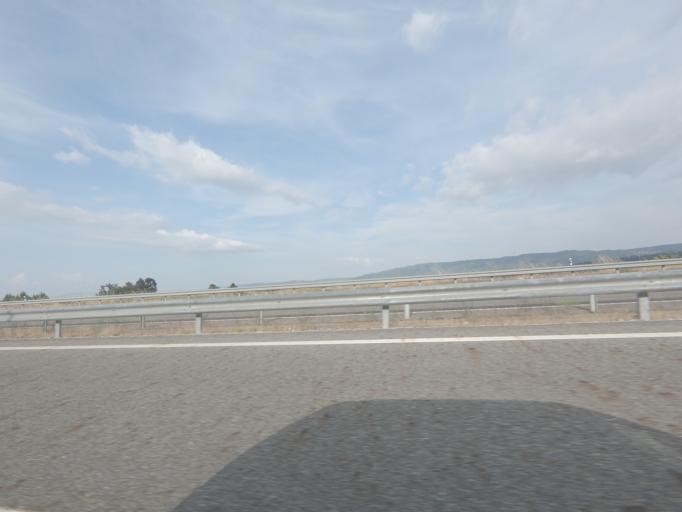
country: PT
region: Vila Real
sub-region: Chaves
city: Chaves
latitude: 41.7148
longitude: -7.5431
